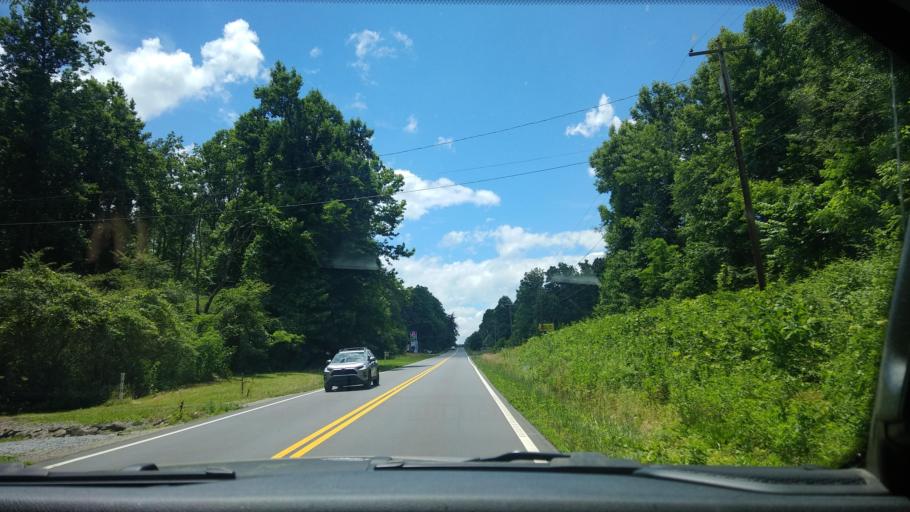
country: US
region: Tennessee
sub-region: Cocke County
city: Newport
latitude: 35.7714
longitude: -83.2696
